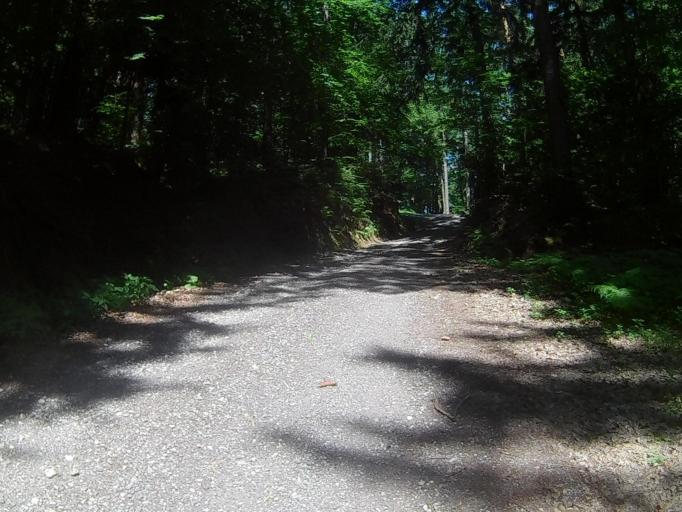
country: SI
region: Race-Fram
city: Fram
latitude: 46.4735
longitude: 15.6200
